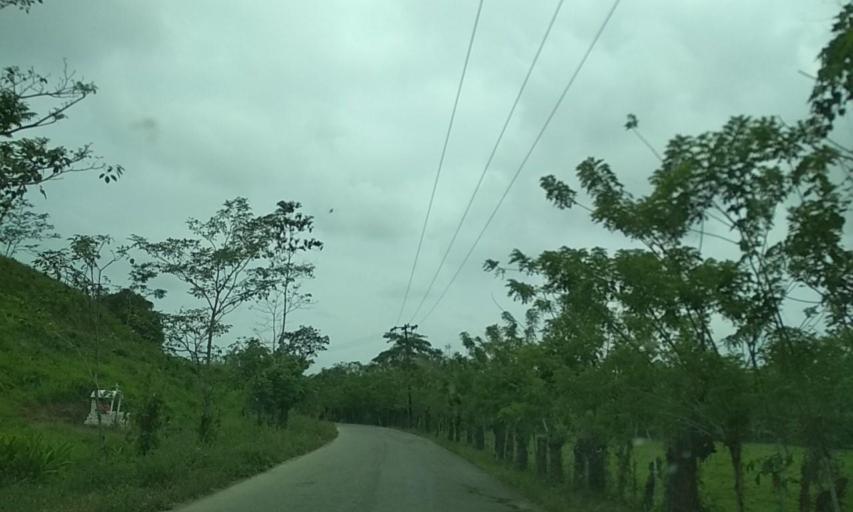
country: MX
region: Veracruz
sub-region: Uxpanapa
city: Poblado 10
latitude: 17.4701
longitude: -94.1164
